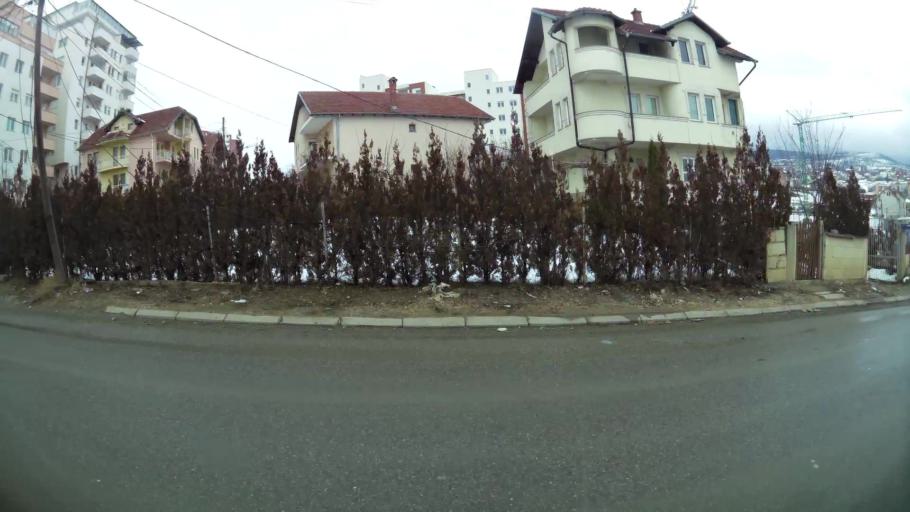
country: XK
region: Pristina
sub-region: Komuna e Prishtines
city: Pristina
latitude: 42.6465
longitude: 21.1829
